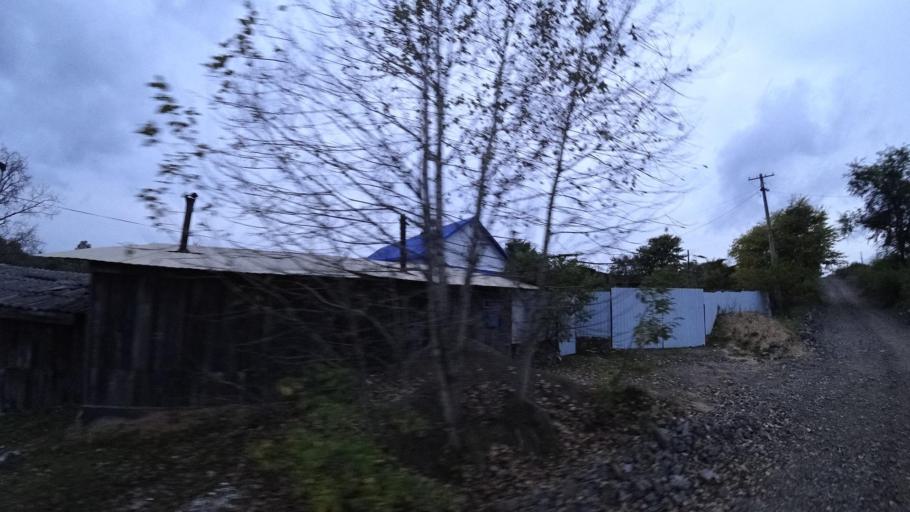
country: RU
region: Jewish Autonomous Oblast
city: Izvestkovyy
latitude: 48.9811
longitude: 131.5545
